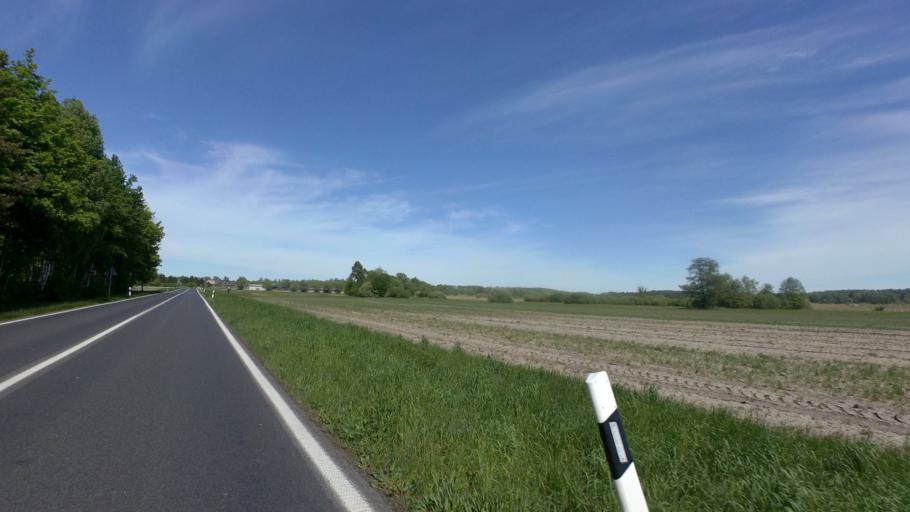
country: DE
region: Brandenburg
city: Sperenberg
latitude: 52.1273
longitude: 13.3671
